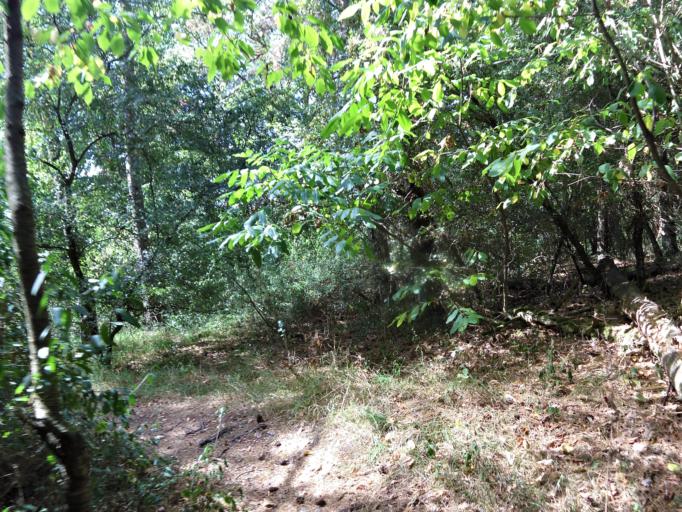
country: DE
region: Bavaria
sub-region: Regierungsbezirk Unterfranken
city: Eibelstadt
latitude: 49.7452
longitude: 10.0034
